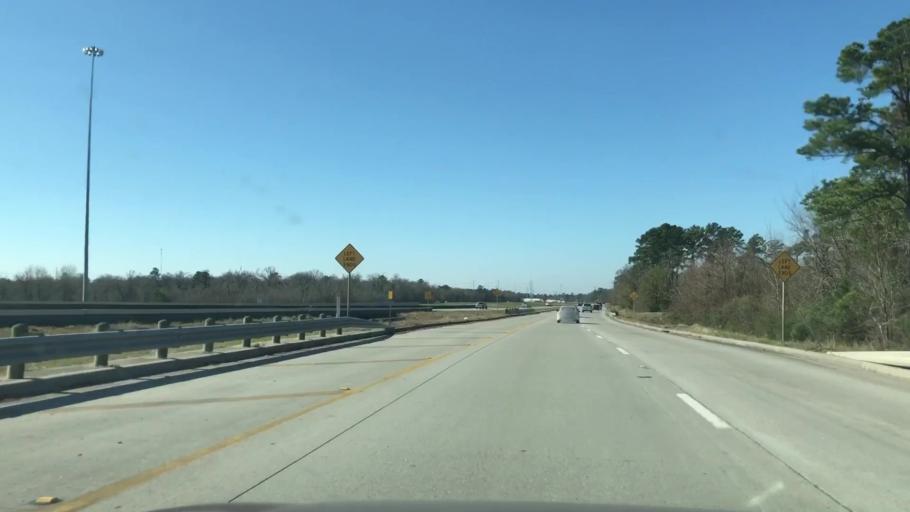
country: US
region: Texas
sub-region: Harris County
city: Cloverleaf
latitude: 29.8284
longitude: -95.1869
